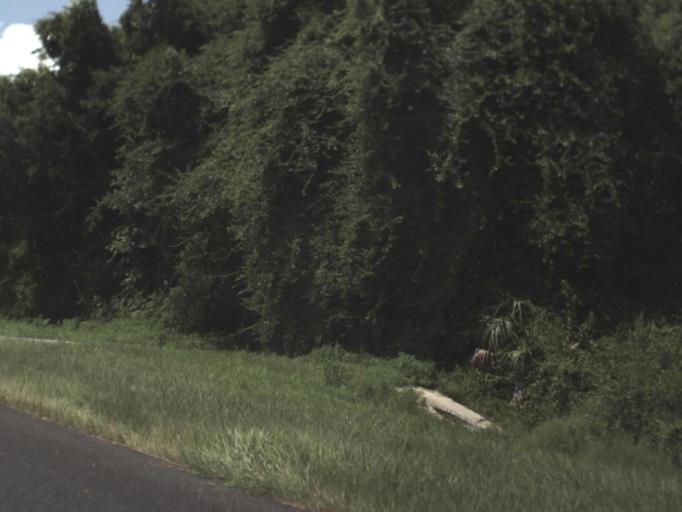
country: US
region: Florida
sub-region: Levy County
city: Inglis
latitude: 29.0222
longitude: -82.6692
